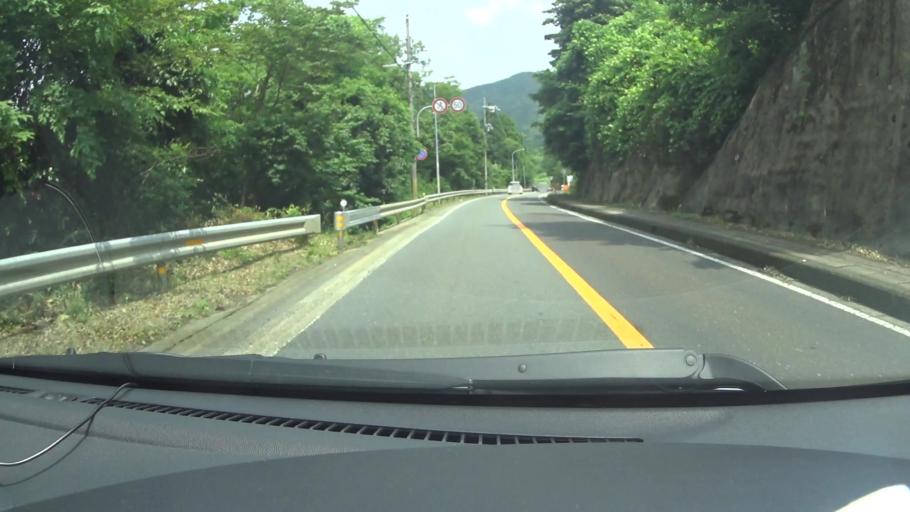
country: JP
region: Kyoto
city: Ayabe
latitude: 35.2941
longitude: 135.3297
